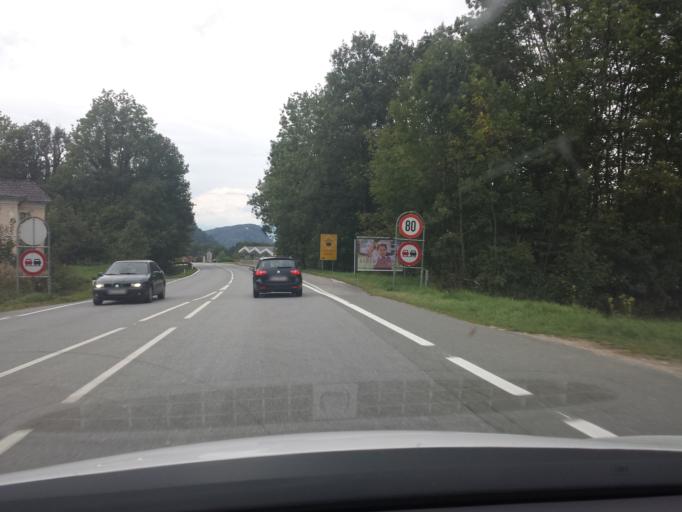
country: AT
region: Salzburg
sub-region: Politischer Bezirk Salzburg-Umgebung
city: Hallwang
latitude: 47.8190
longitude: 13.0989
